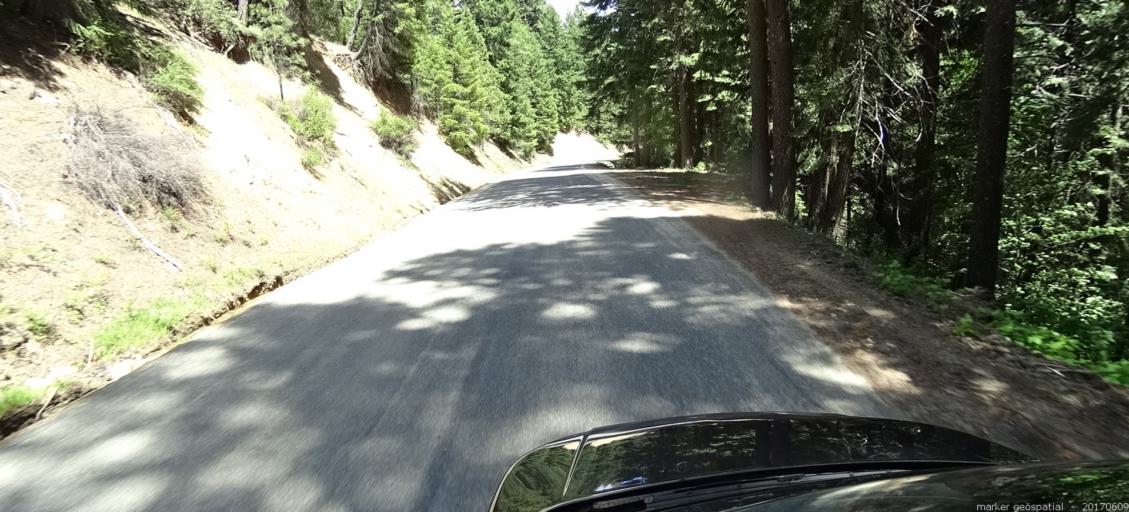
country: US
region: California
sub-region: Siskiyou County
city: Yreka
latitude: 41.4294
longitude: -122.9560
